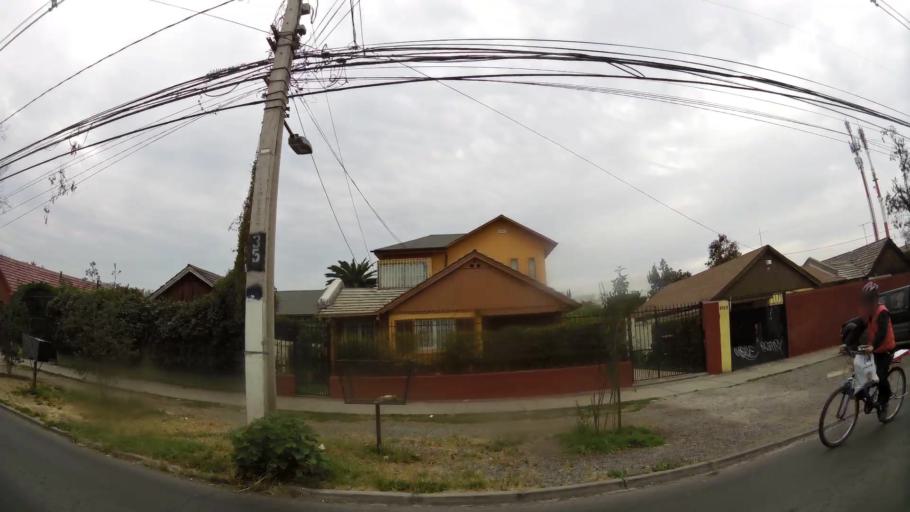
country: CL
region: Santiago Metropolitan
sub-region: Provincia de Santiago
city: Villa Presidente Frei, Nunoa, Santiago, Chile
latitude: -33.4796
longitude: -70.5959
